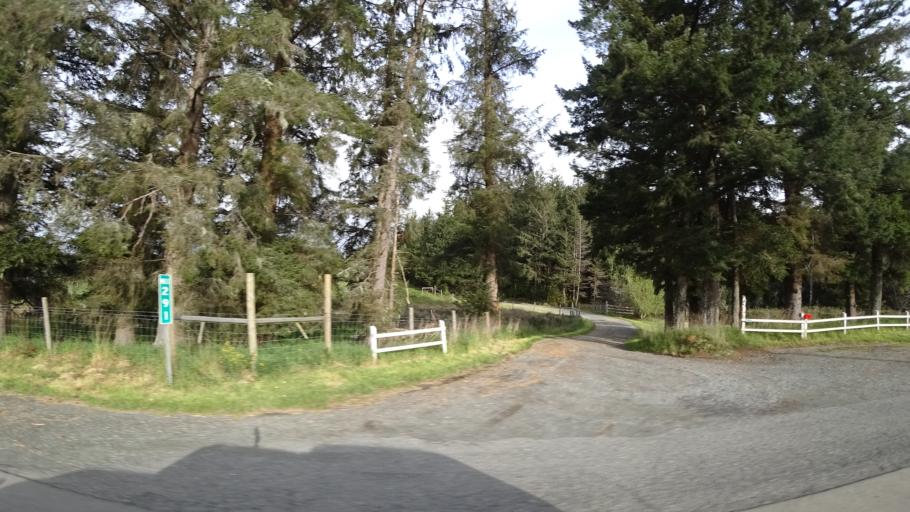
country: US
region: Oregon
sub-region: Curry County
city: Port Orford
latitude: 42.8823
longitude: -124.4650
